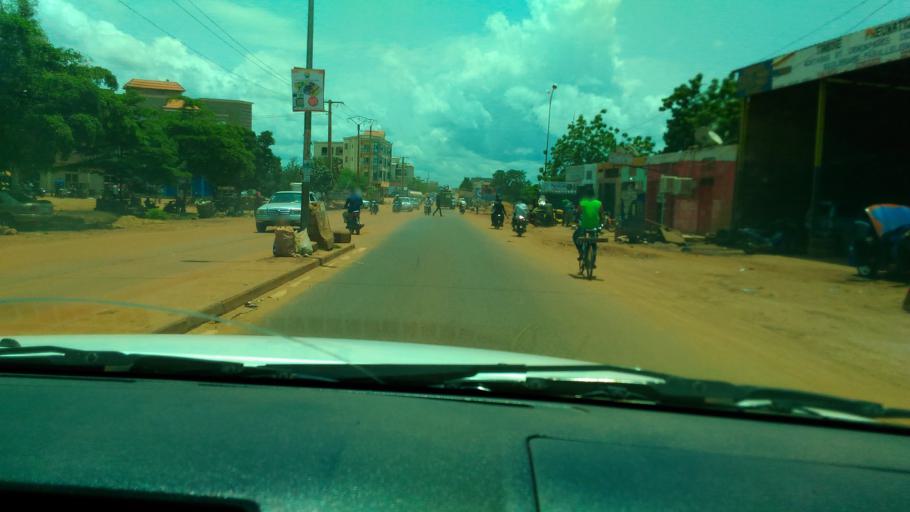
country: ML
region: Bamako
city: Bamako
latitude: 12.6701
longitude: -7.9186
